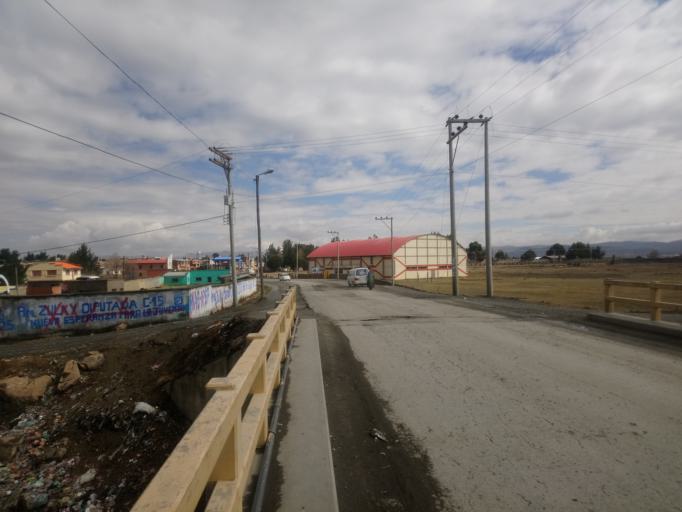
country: BO
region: La Paz
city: Achacachi
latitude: -16.0381
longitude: -68.6867
